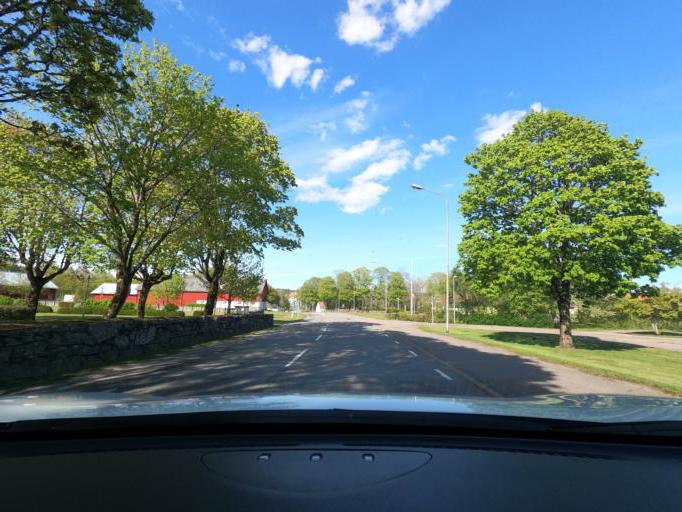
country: SE
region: Vaestra Goetaland
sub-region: Harryda Kommun
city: Ravlanda
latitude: 57.6505
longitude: 12.4915
